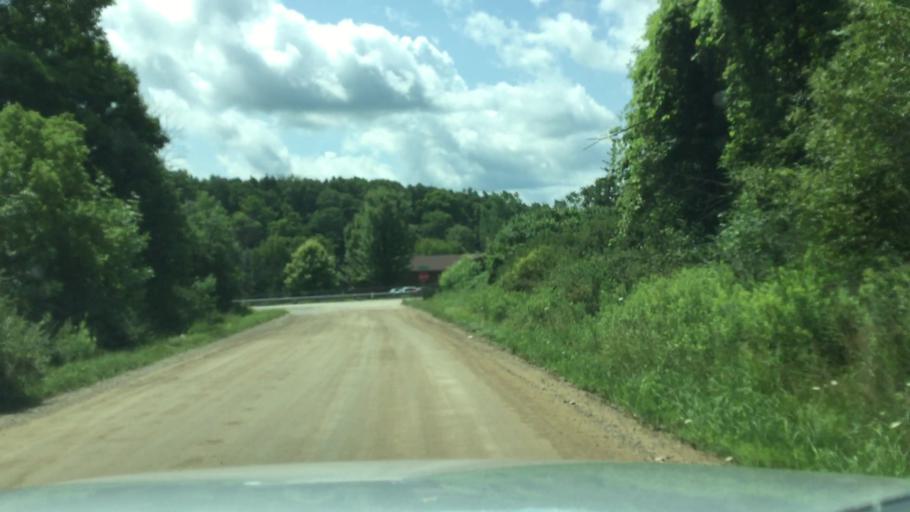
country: US
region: Michigan
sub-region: Ionia County
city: Belding
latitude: 43.1109
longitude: -85.2063
